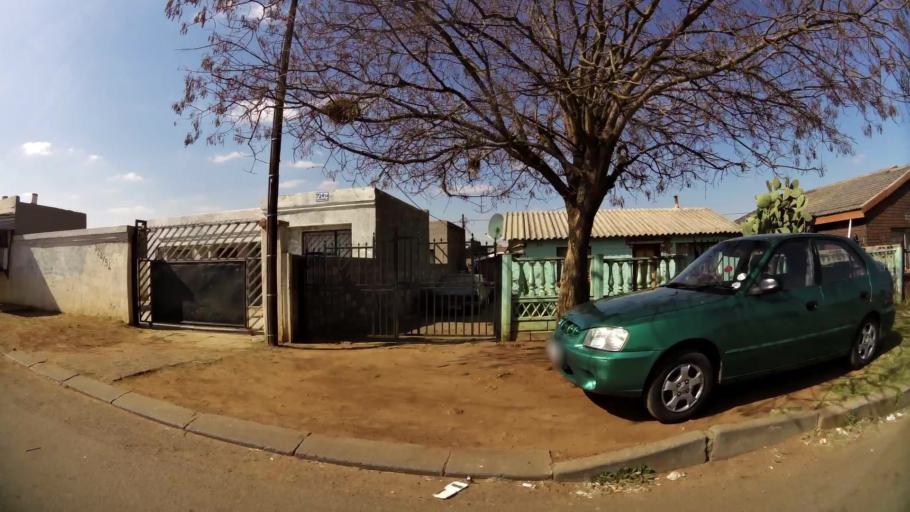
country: ZA
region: Gauteng
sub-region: City of Johannesburg Metropolitan Municipality
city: Soweto
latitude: -26.2564
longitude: 27.8883
